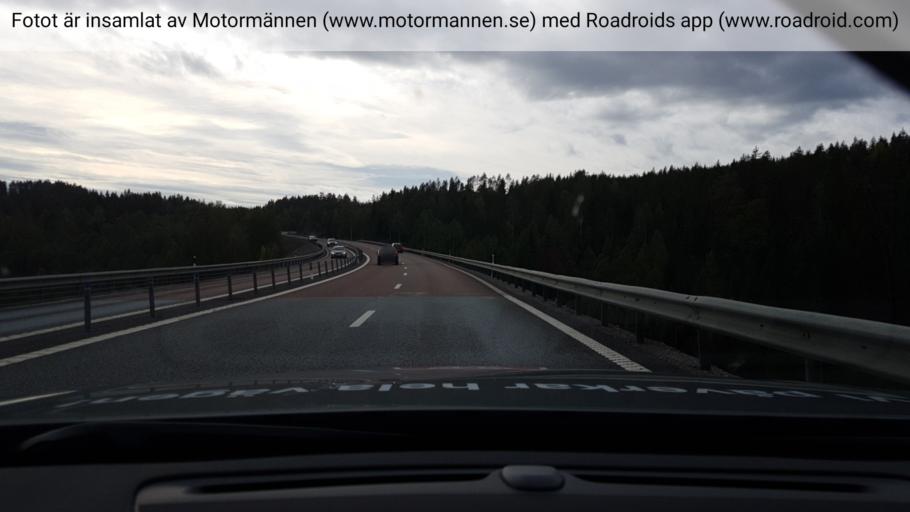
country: SE
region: Vaermland
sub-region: Arjangs Kommun
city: Toecksfors
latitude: 59.4949
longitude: 11.7760
